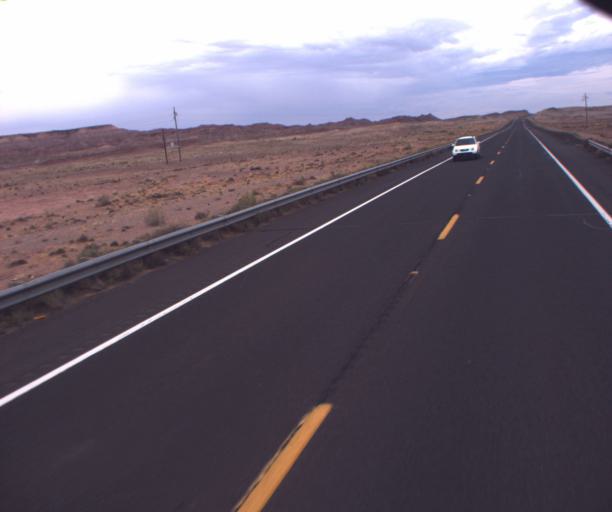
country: US
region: Arizona
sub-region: Coconino County
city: Tuba City
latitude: 36.0099
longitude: -111.3949
